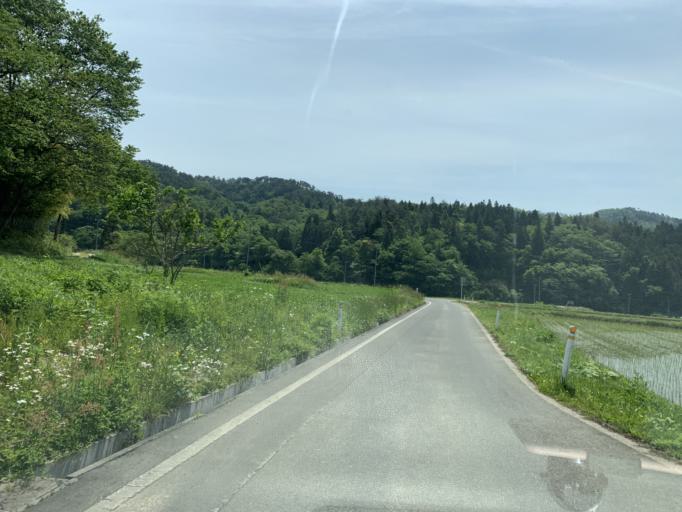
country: JP
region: Iwate
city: Ichinoseki
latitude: 38.9720
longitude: 141.2189
